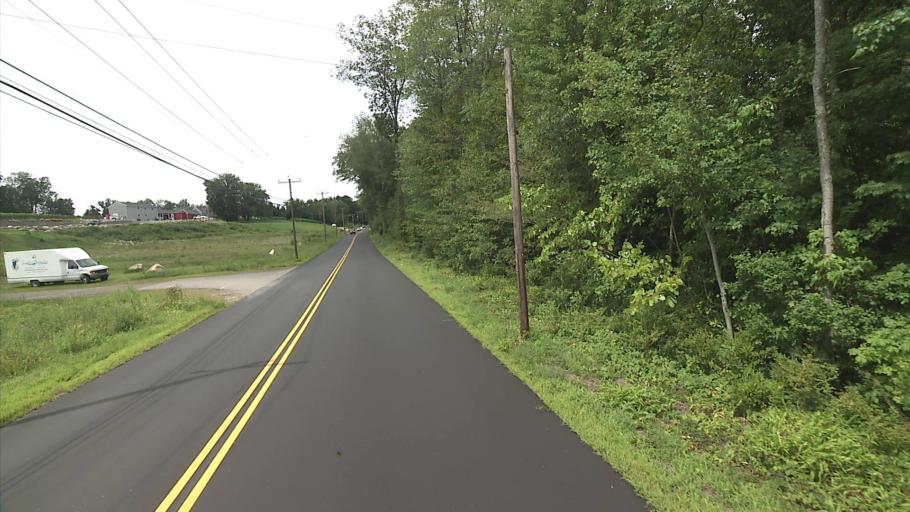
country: US
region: Connecticut
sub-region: Windham County
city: South Woodstock
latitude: 41.9458
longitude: -72.0069
